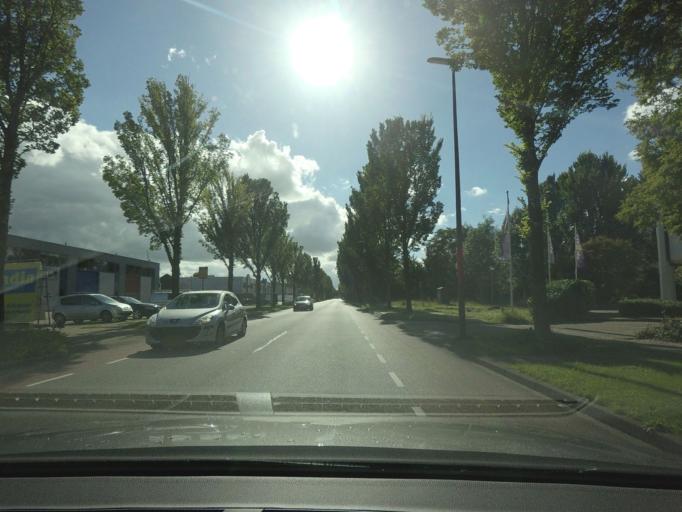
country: NL
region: North Holland
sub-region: Gemeente Langedijk
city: Broek op Langedijk
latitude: 52.6521
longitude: 4.7887
